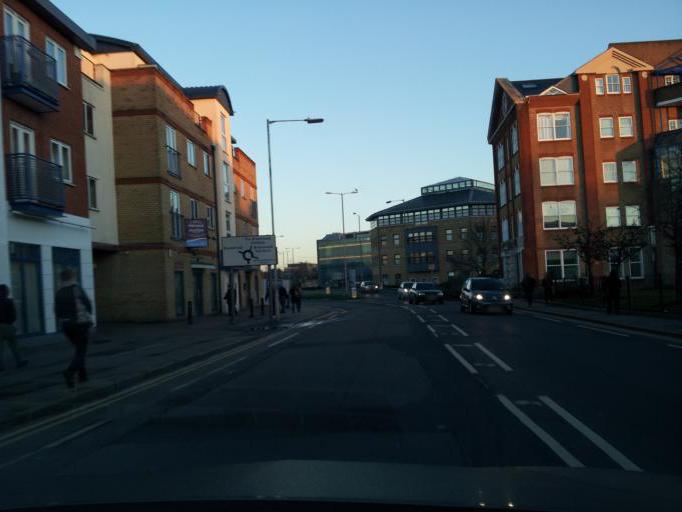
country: GB
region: England
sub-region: Essex
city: Chelmsford
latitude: 51.7400
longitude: 0.4740
